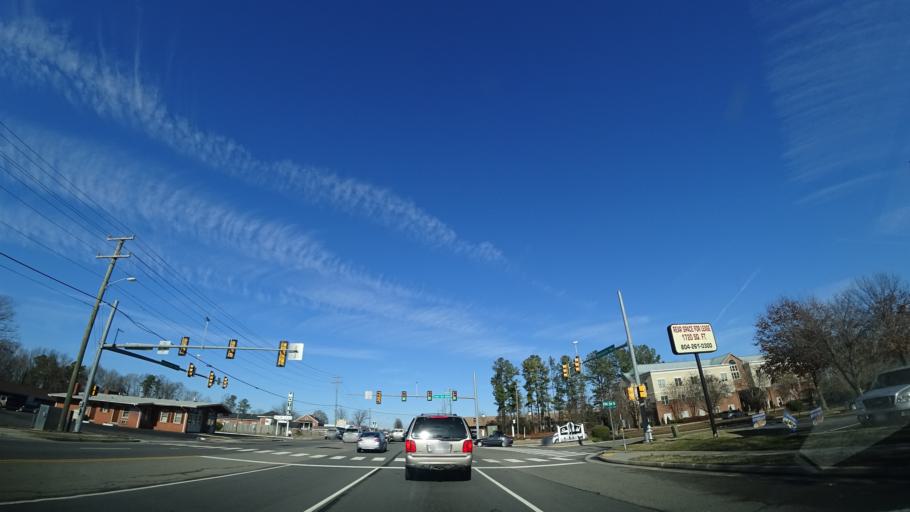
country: US
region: Virginia
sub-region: Hanover County
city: Ashland
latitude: 37.7532
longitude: -77.4714
